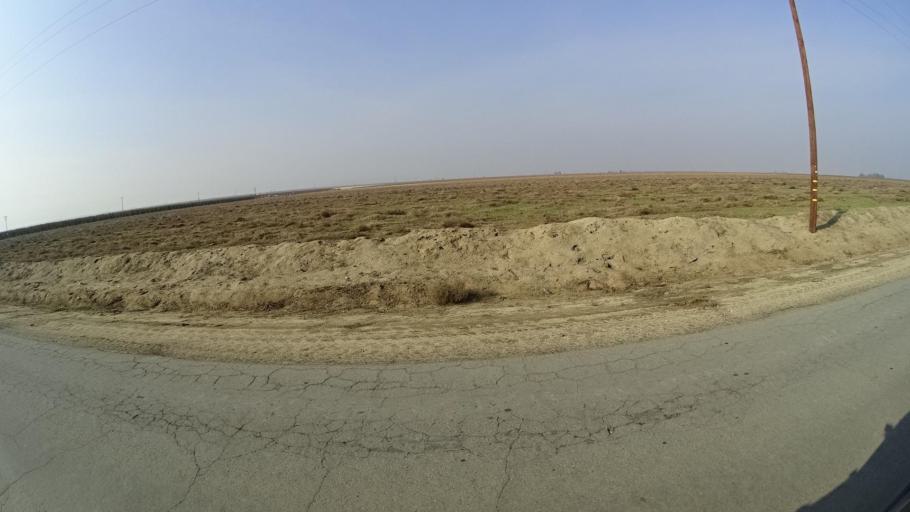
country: US
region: California
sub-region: Kern County
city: Arvin
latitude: 35.0325
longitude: -118.8466
